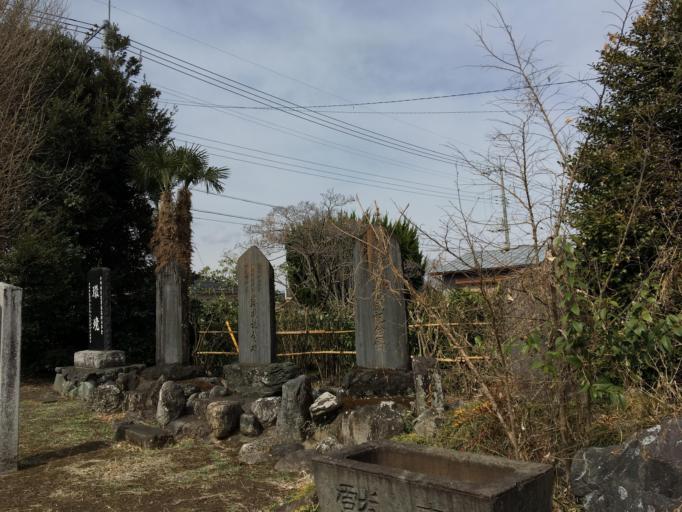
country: JP
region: Saitama
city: Yorii
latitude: 36.1363
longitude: 139.2137
